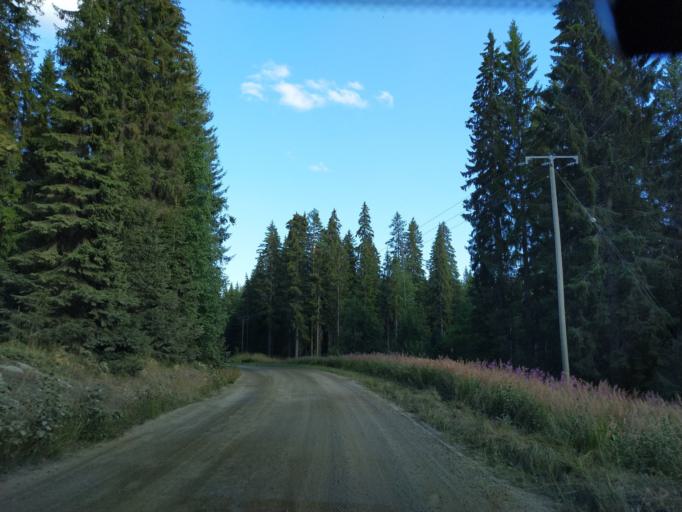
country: FI
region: Central Finland
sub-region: Jaemsae
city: Kuhmoinen
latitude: 61.6966
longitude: 24.9274
